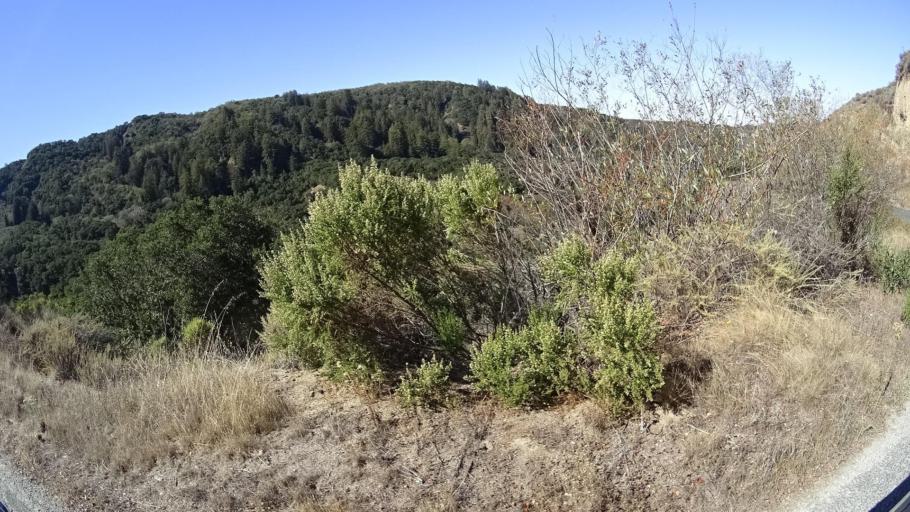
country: US
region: California
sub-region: Monterey County
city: Carmel Valley Village
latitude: 36.4798
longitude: -121.8036
